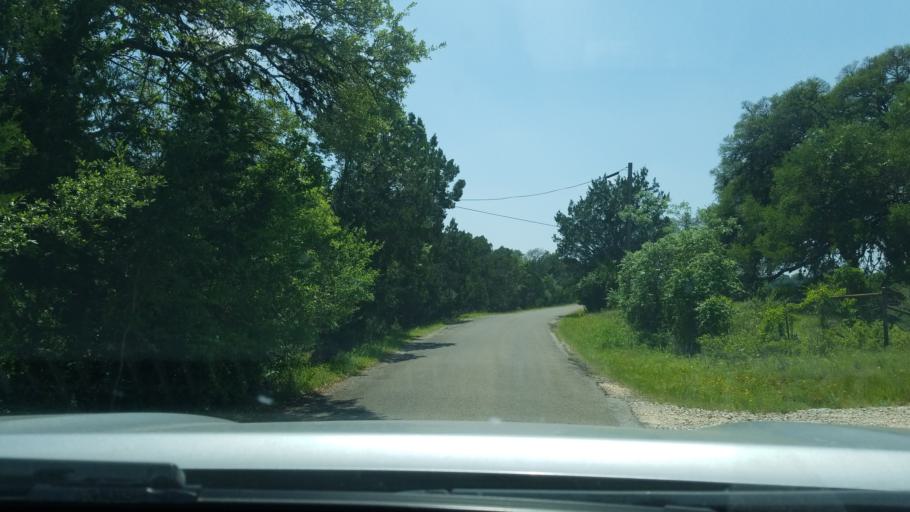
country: US
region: Texas
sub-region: Blanco County
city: Blanco
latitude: 30.0006
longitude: -98.4157
